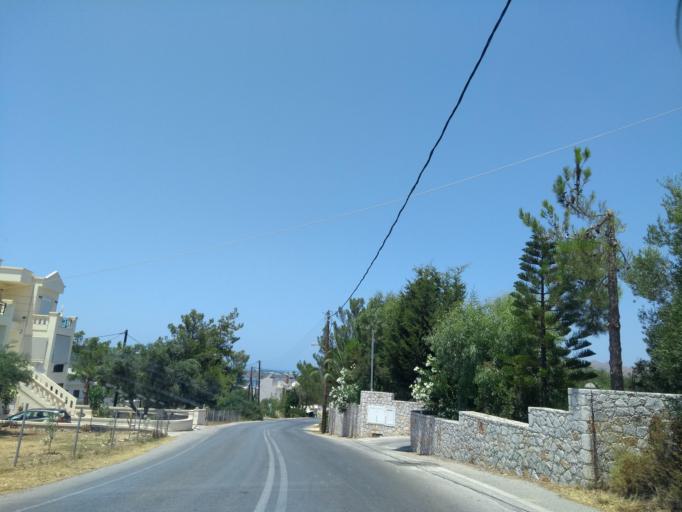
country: GR
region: Crete
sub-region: Nomos Chanias
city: Pithari
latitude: 35.5453
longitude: 24.0825
